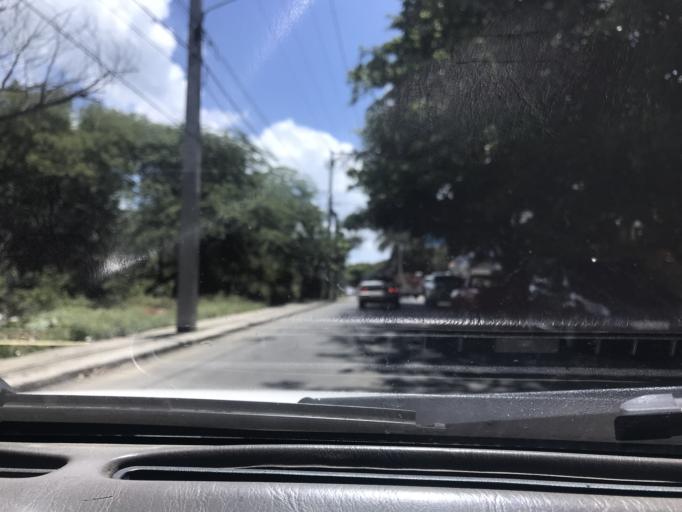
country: DO
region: Santiago
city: Santiago de los Caballeros
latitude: 19.4262
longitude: -70.7023
